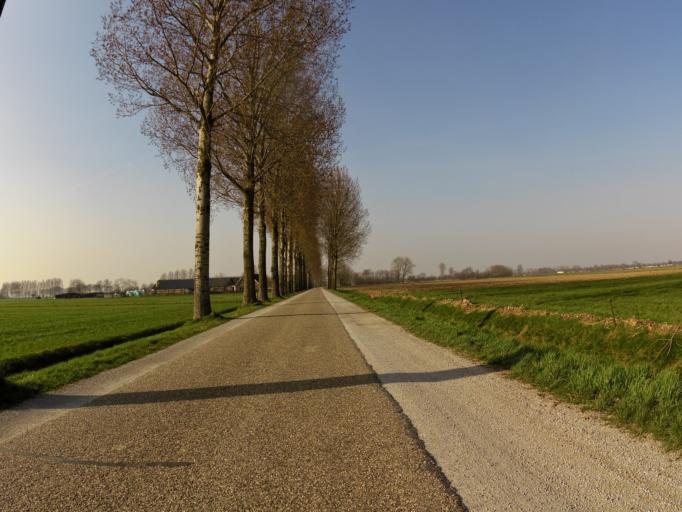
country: NL
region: North Brabant
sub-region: Gemeente Aalburg
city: Aalburg
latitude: 51.7592
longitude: 5.0777
